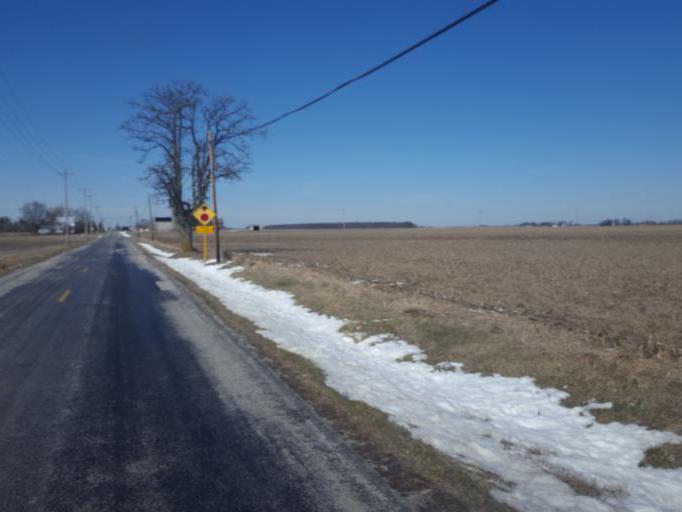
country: US
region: Ohio
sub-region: Marion County
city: Marion
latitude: 40.6588
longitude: -83.2224
